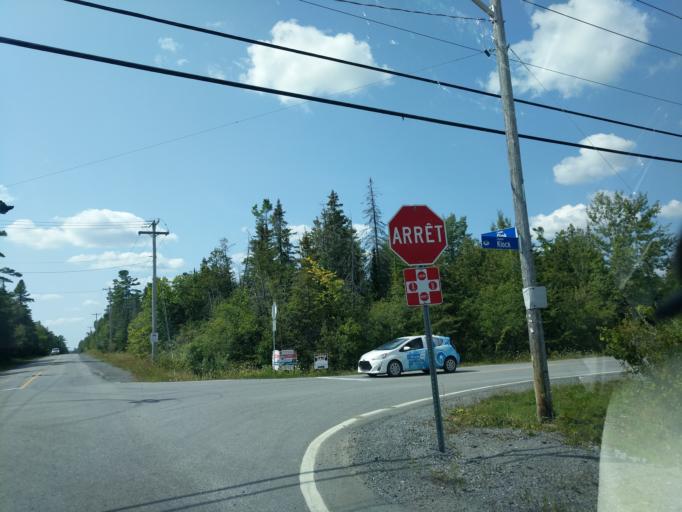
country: CA
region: Ontario
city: Bells Corners
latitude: 45.4394
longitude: -75.8533
